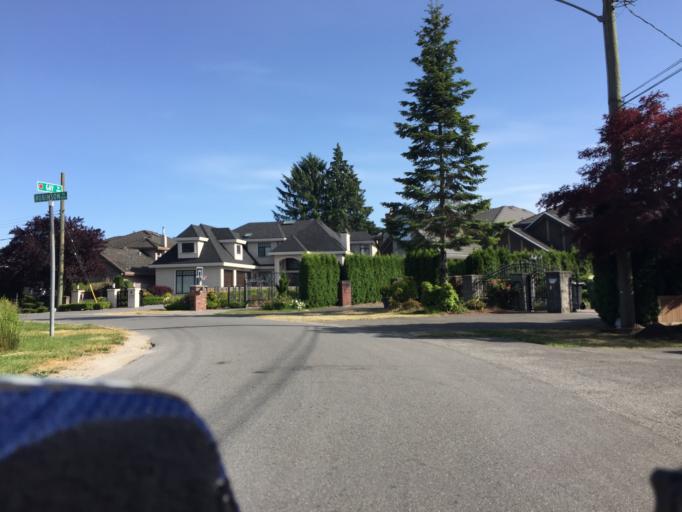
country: CA
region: British Columbia
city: Richmond
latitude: 49.1496
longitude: -123.1351
